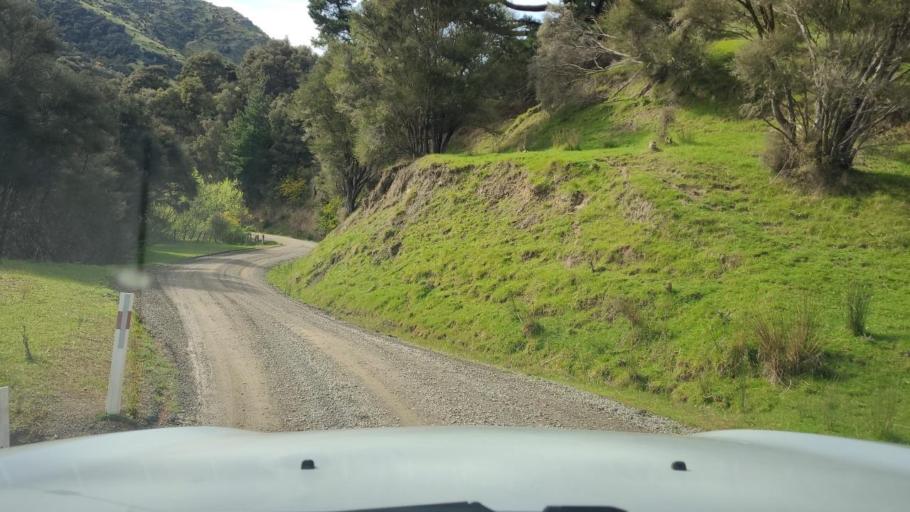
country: NZ
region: Wellington
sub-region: South Wairarapa District
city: Waipawa
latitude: -41.3252
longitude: 175.6576
